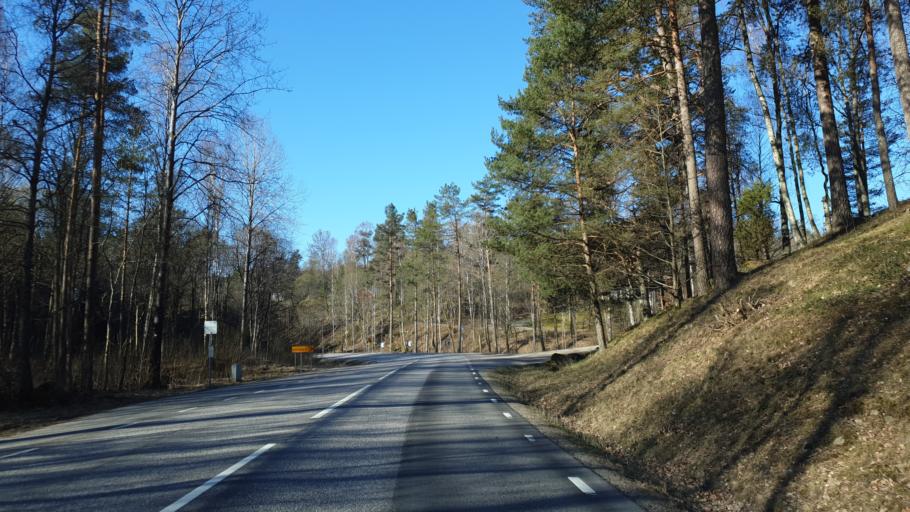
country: SE
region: Vaestra Goetaland
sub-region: Boras Kommun
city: Dalsjofors
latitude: 57.7477
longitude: 13.1082
